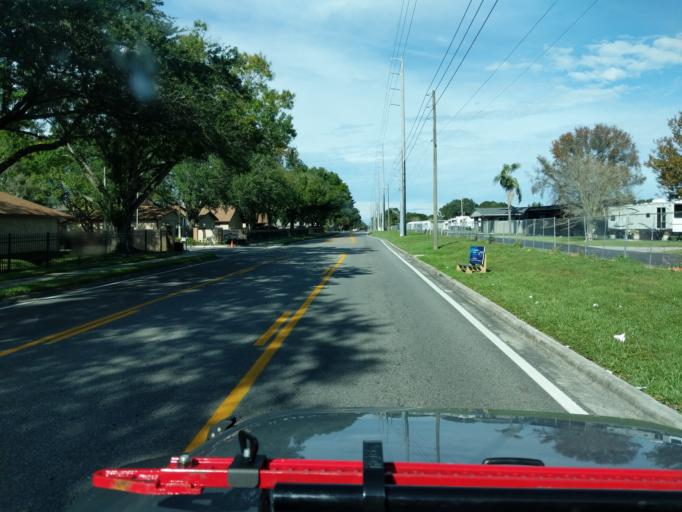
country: US
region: Florida
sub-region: Orange County
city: Winter Garden
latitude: 28.5531
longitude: -81.5918
